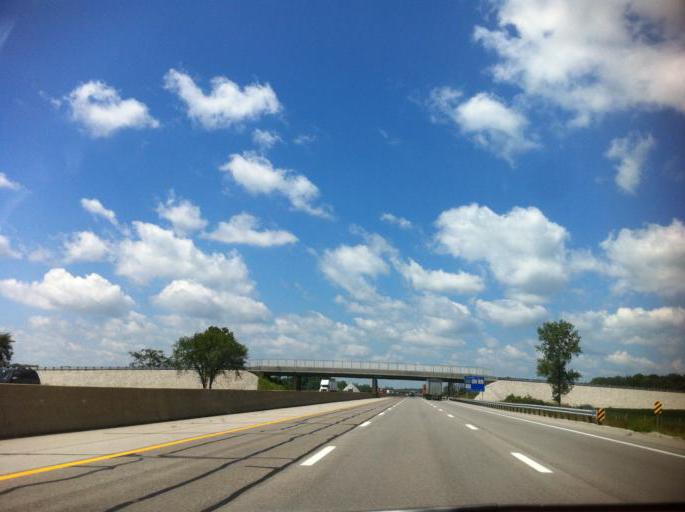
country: US
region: Ohio
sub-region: Sandusky County
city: Fremont
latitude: 41.3927
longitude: -83.0752
